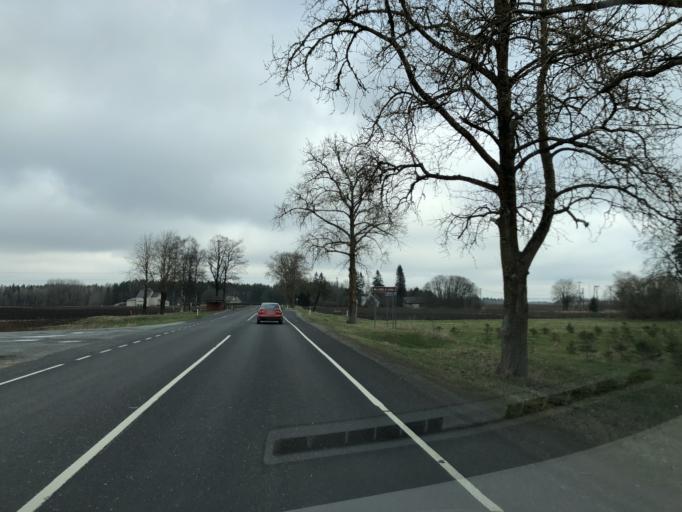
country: EE
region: Laeaene-Virumaa
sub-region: Rakvere linn
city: Rakvere
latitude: 59.2693
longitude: 26.2845
